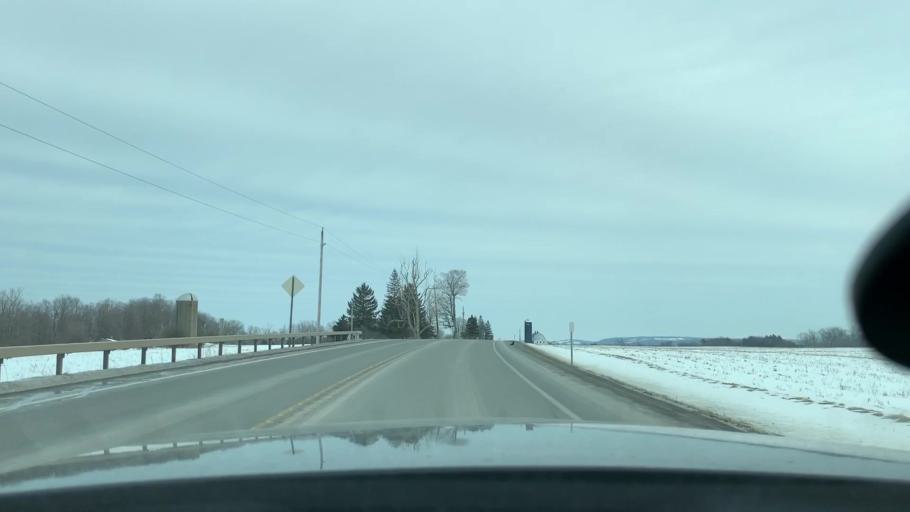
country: US
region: New York
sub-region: Herkimer County
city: Frankfort
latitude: 43.0337
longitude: -75.1295
